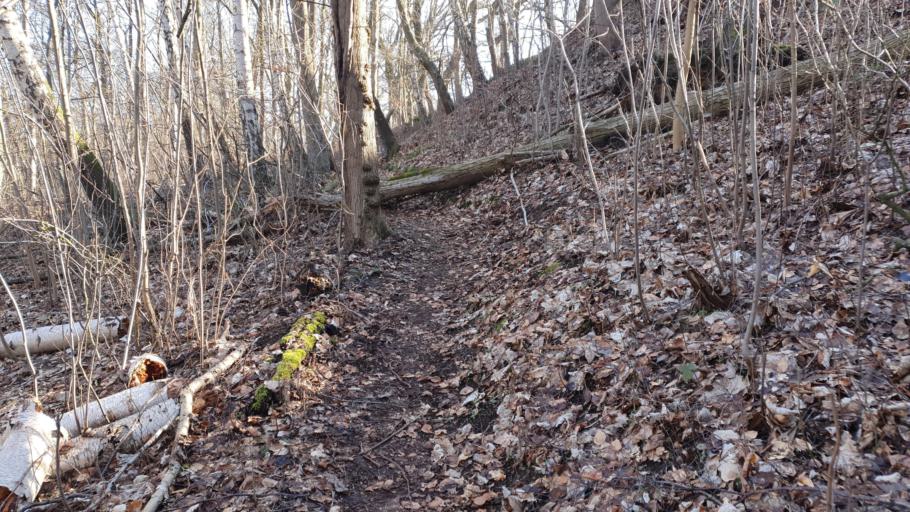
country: DE
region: Mecklenburg-Vorpommern
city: Wittenforden
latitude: 53.6461
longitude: 11.3238
